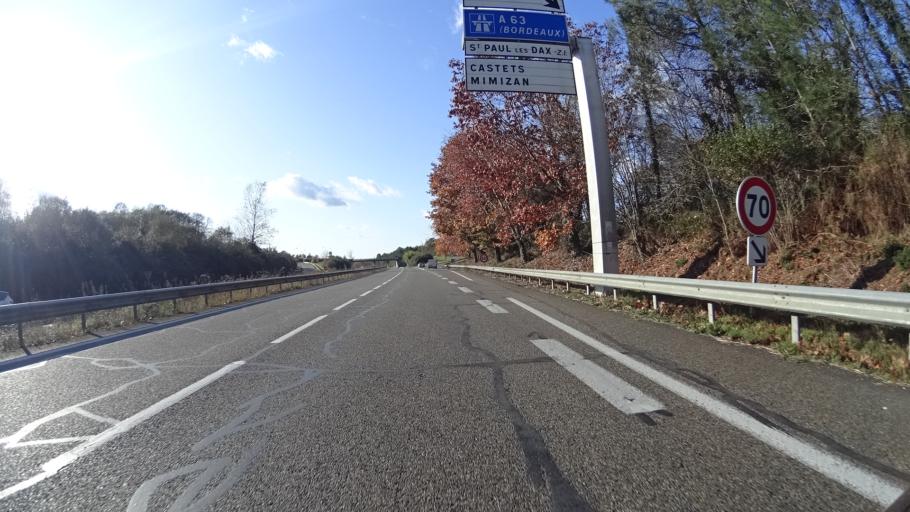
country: FR
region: Aquitaine
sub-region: Departement des Landes
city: Saint-Paul-les-Dax
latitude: 43.7446
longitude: -1.0518
